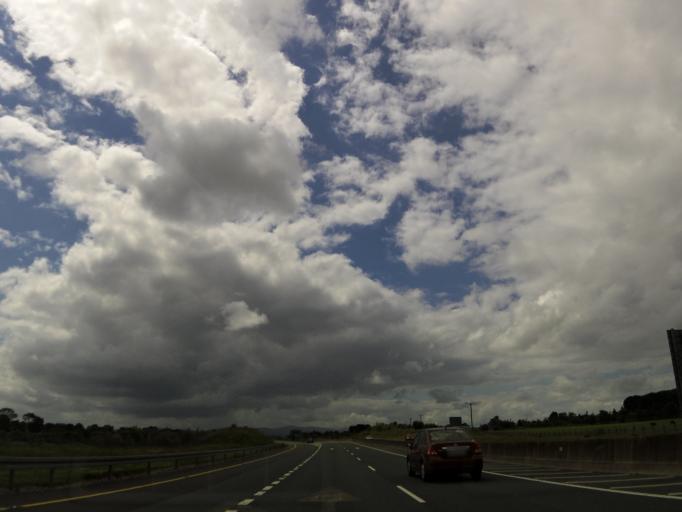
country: IE
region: Munster
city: Cashel
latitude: 52.5025
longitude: -7.8820
